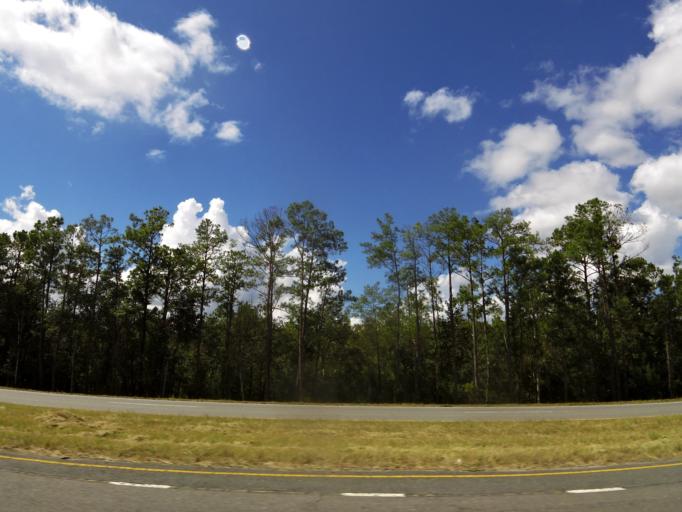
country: US
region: Georgia
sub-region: Charlton County
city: Folkston
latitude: 30.7789
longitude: -81.9788
